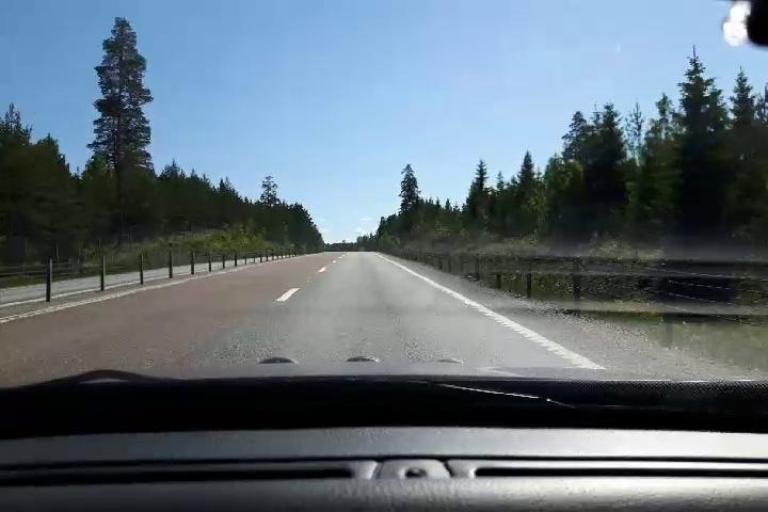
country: SE
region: Gaevleborg
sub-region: Soderhamns Kommun
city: Ljusne
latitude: 61.1351
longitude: 17.0223
